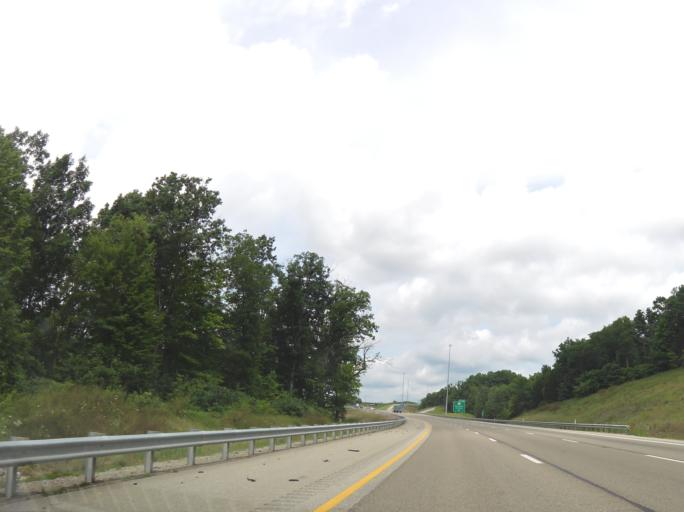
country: US
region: Kentucky
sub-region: Grant County
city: Williamstown
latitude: 38.4826
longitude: -84.5806
